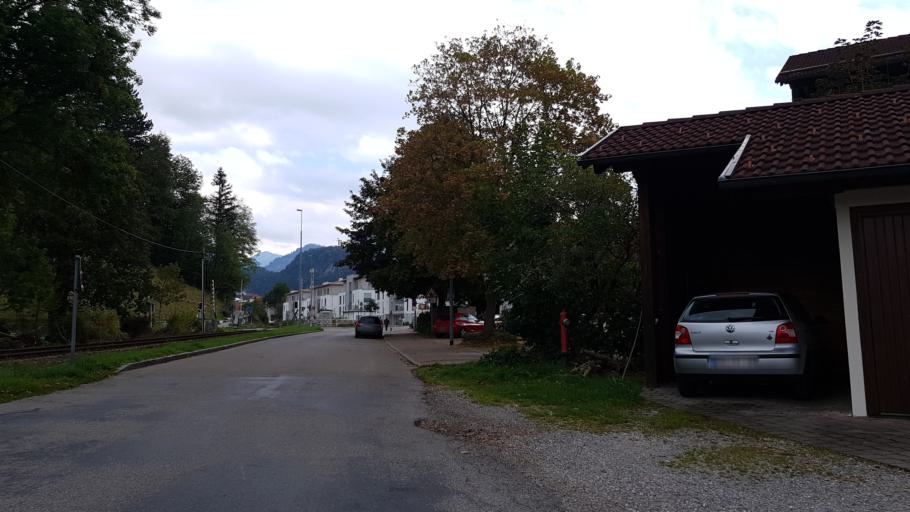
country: DE
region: Bavaria
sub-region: Swabia
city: Fuessen
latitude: 47.5723
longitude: 10.6915
